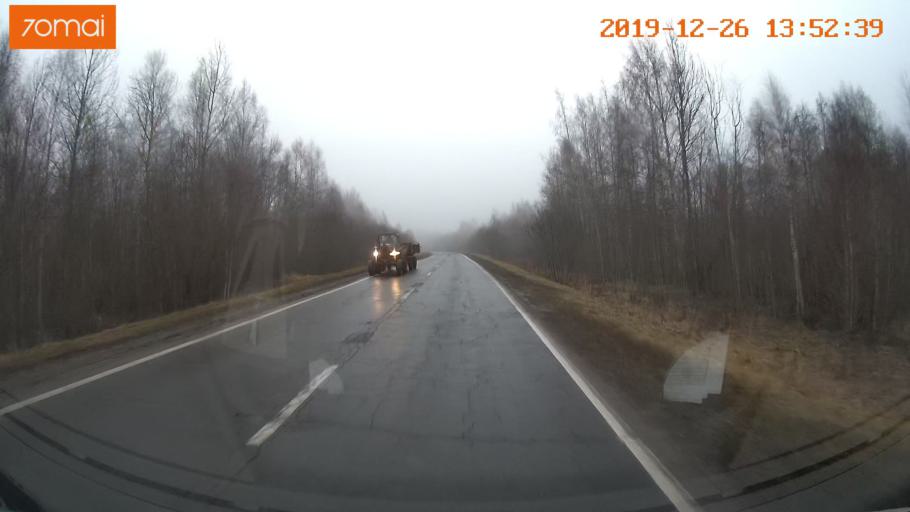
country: RU
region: Jaroslavl
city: Poshekhon'ye
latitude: 58.6292
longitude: 38.6037
